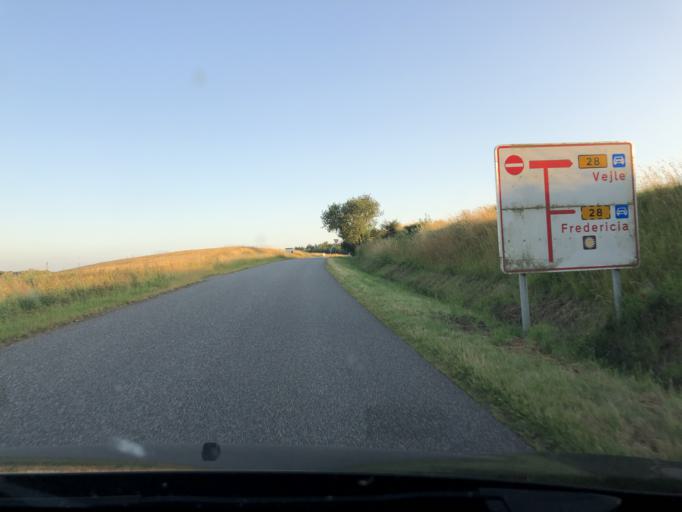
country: DK
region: South Denmark
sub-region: Fredericia Kommune
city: Fredericia
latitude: 55.6272
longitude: 9.7349
